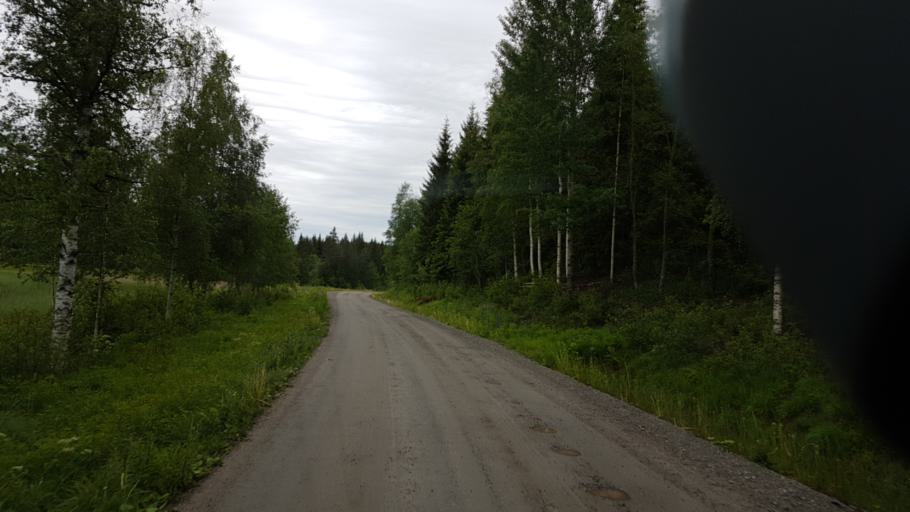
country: NO
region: Ostfold
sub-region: Romskog
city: Romskog
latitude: 59.6733
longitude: 11.9335
